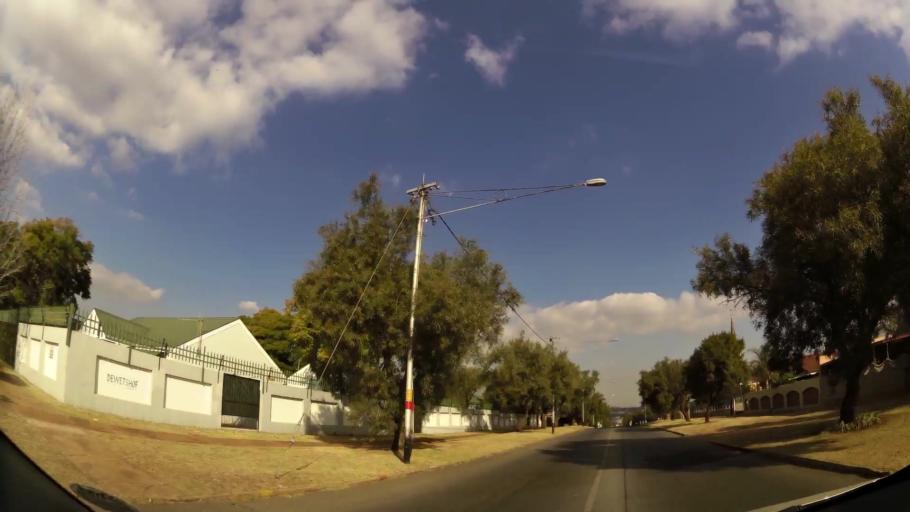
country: ZA
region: Gauteng
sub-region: West Rand District Municipality
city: Krugersdorp
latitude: -26.0863
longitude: 27.7704
